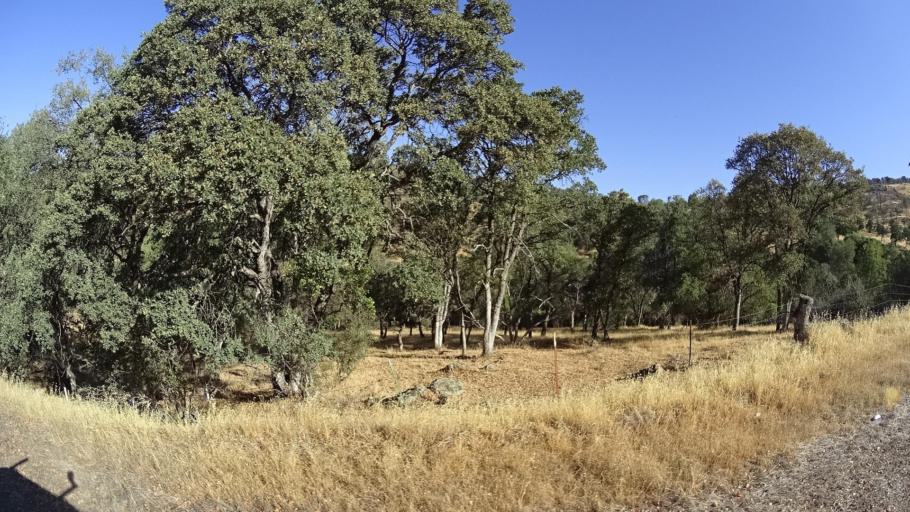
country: US
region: California
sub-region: Mariposa County
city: Mariposa
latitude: 37.5581
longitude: -120.1698
